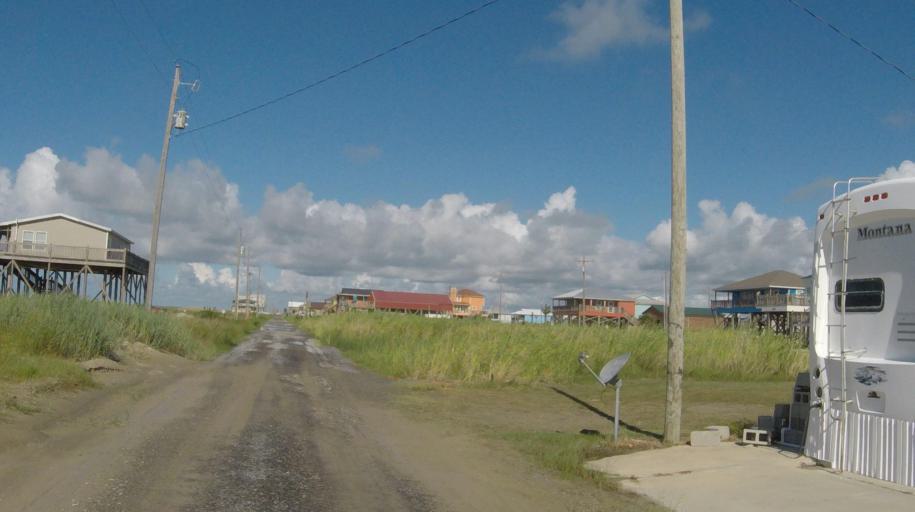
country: US
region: Louisiana
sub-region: Cameron Parish
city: Cameron
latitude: 29.7700
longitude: -93.4498
